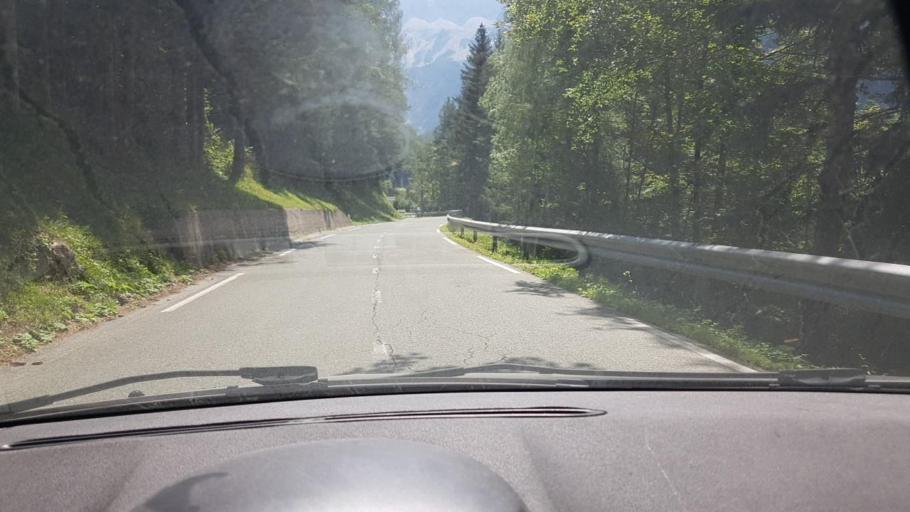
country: SI
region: Jezersko
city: Zgornje Jezersko
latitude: 46.4085
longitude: 14.5263
